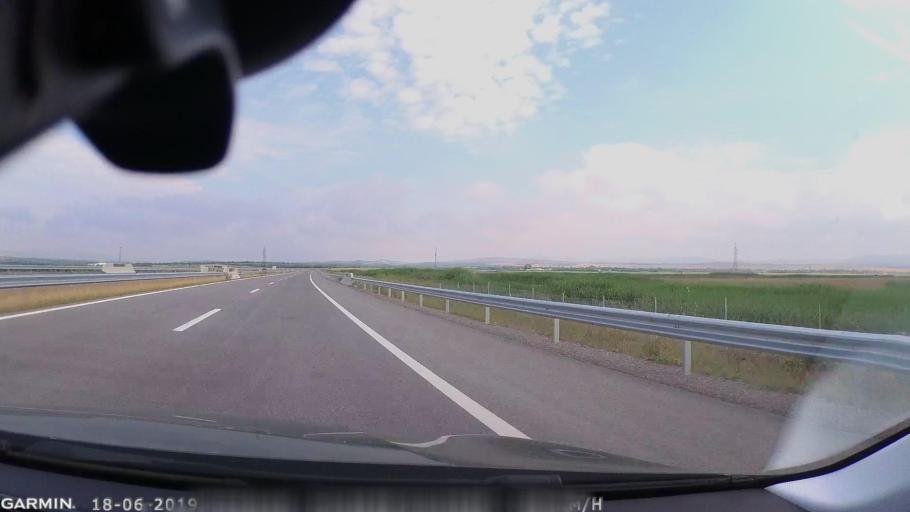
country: MK
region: Sveti Nikole
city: Sveti Nikole
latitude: 41.8188
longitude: 22.0156
